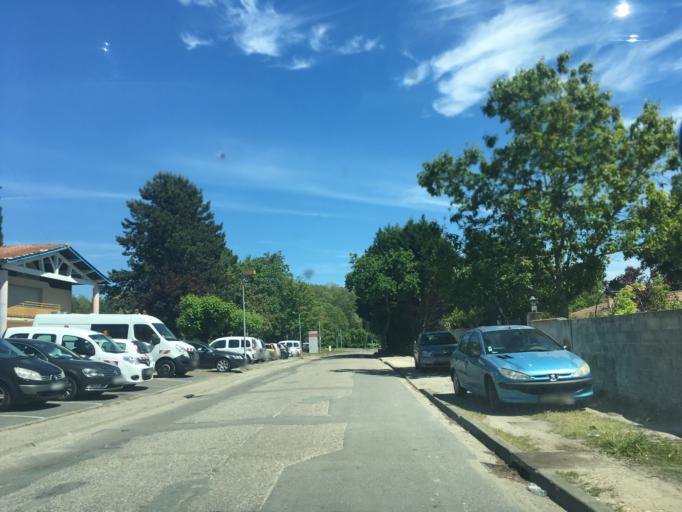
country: FR
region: Aquitaine
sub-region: Departement de la Gironde
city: Castelnau-de-Medoc
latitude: 45.0365
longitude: -0.8010
